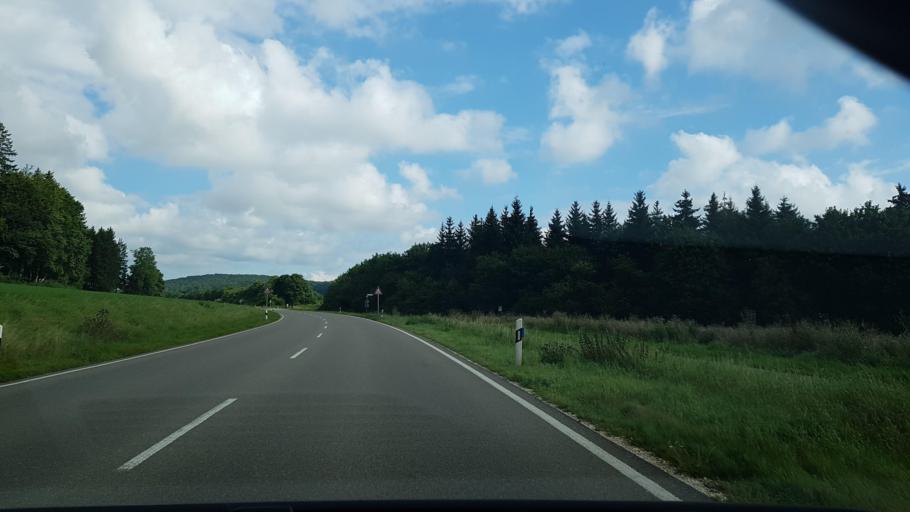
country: DE
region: Baden-Wuerttemberg
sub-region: Tuebingen Region
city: Westerheim
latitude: 48.4777
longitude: 9.5916
